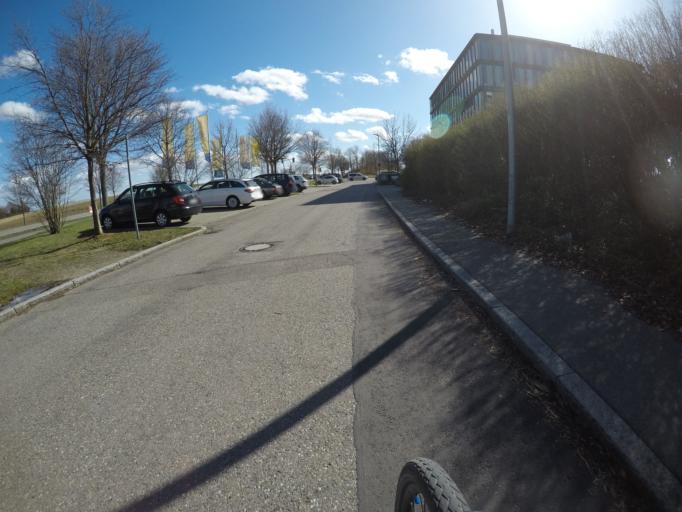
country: DE
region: Baden-Wuerttemberg
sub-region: Regierungsbezirk Stuttgart
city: Leinfelden-Echterdingen
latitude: 48.7068
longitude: 9.1491
